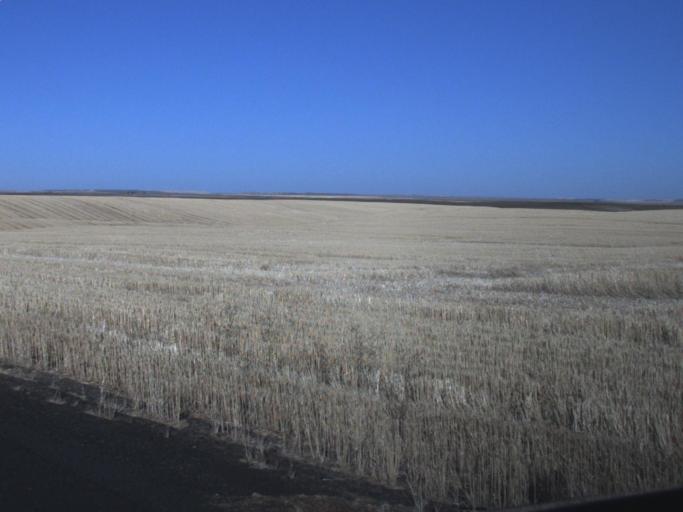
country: US
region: Washington
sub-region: Adams County
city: Ritzville
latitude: 46.8854
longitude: -118.3345
